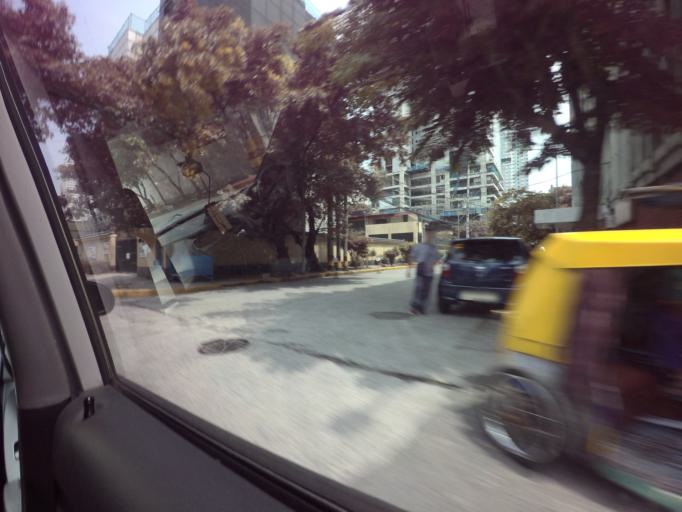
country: PH
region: Metro Manila
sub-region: City of Manila
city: Port Area
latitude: 14.5731
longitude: 120.9882
